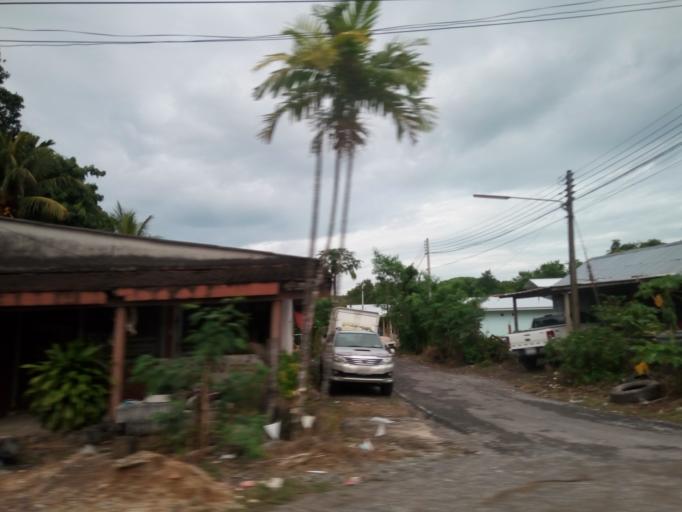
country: TH
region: Phuket
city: Thalang
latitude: 8.0947
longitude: 98.3378
